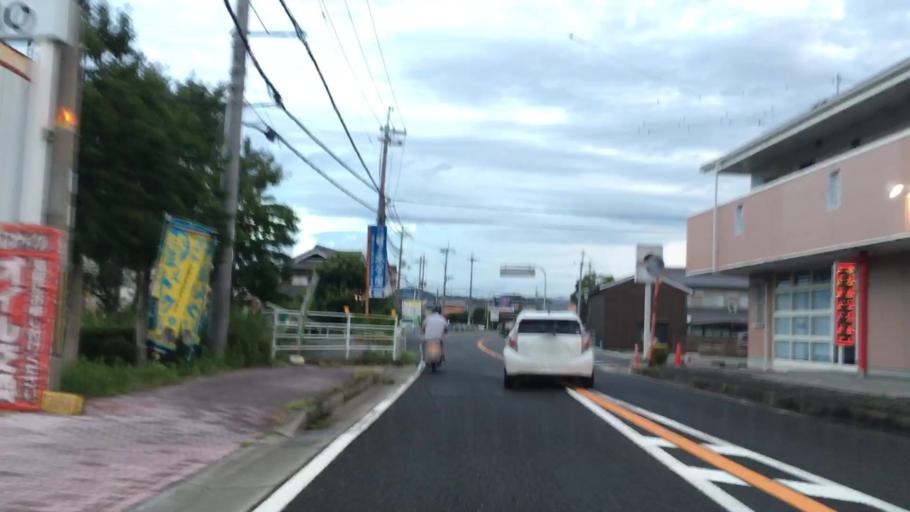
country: JP
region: Hyogo
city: Himeji
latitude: 34.9114
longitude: 134.7390
